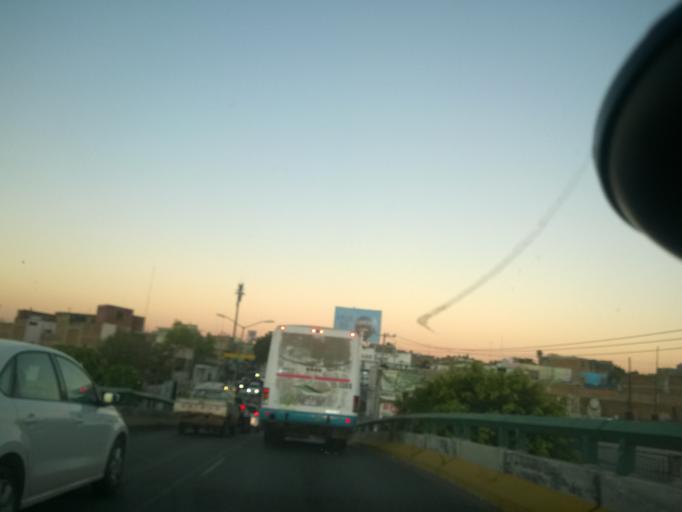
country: MX
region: Guanajuato
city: Leon
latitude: 21.1167
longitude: -101.6892
